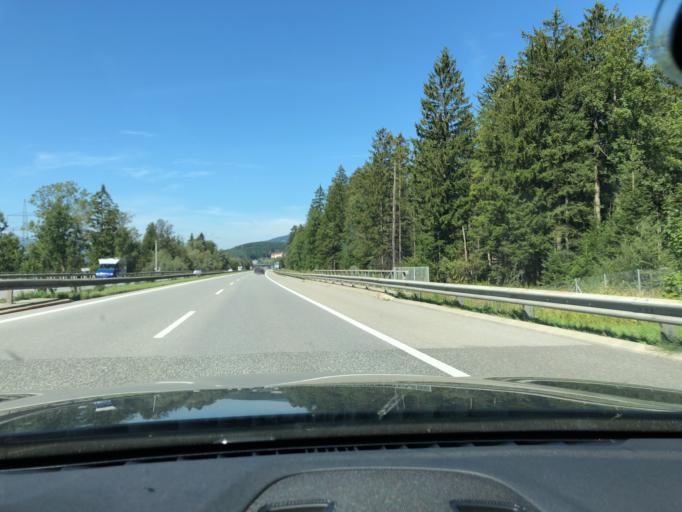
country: AT
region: Vorarlberg
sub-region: Politischer Bezirk Bludenz
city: Bludesch
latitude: 47.1829
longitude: 9.7258
